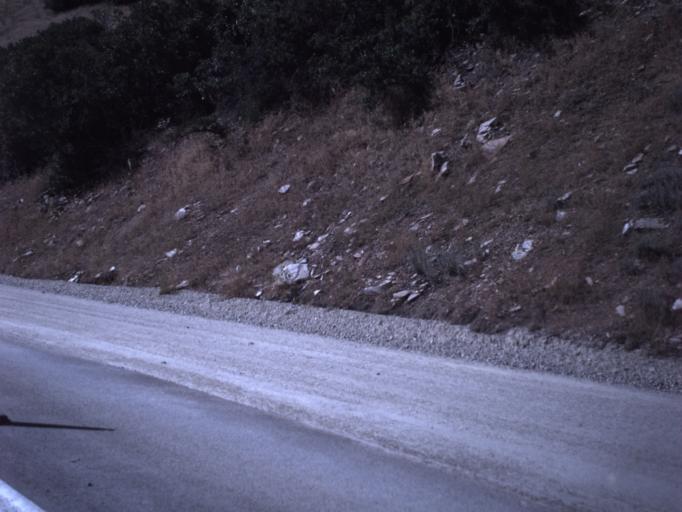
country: US
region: Utah
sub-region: Wasatch County
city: Heber
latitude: 40.4114
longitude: -111.3208
